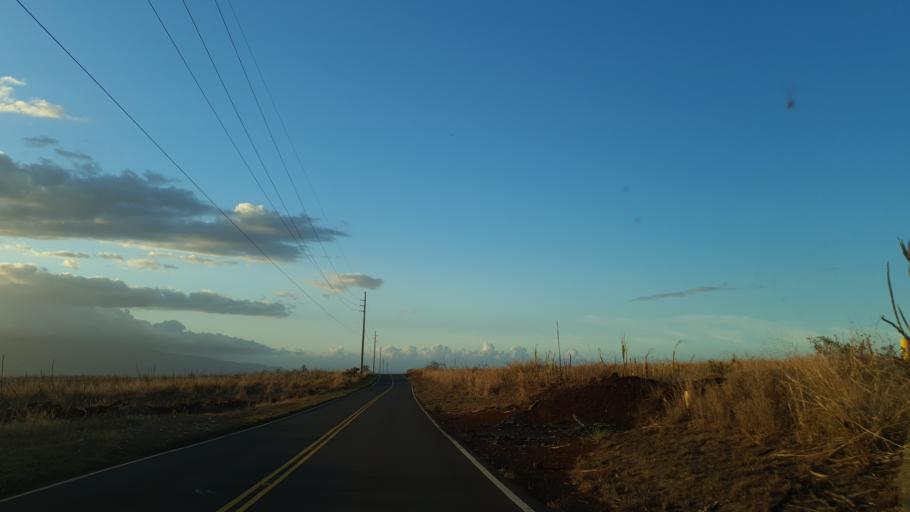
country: US
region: Hawaii
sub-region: Maui County
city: Pukalani
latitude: 20.8061
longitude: -156.3793
